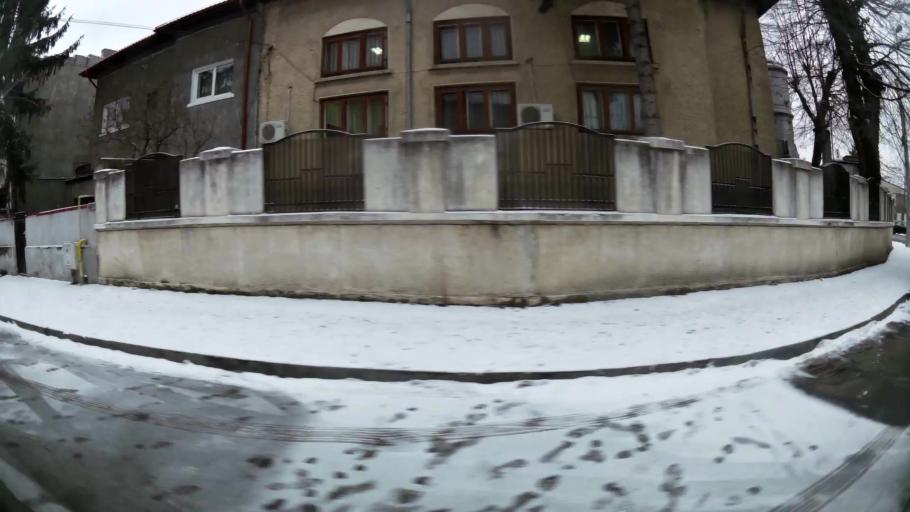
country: RO
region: Prahova
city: Ploiesti
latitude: 44.9392
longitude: 26.0299
